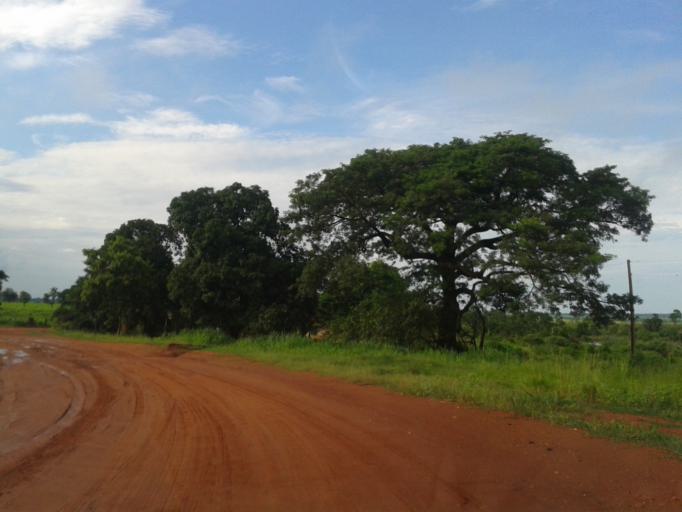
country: BR
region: Minas Gerais
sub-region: Santa Vitoria
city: Santa Vitoria
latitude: -19.1372
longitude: -50.5573
